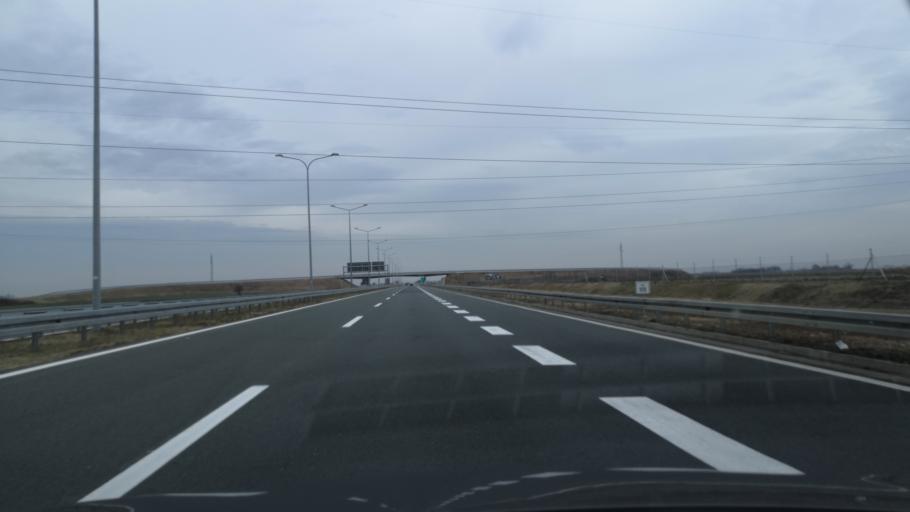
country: RS
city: Rumenka
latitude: 45.3150
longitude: 19.7973
